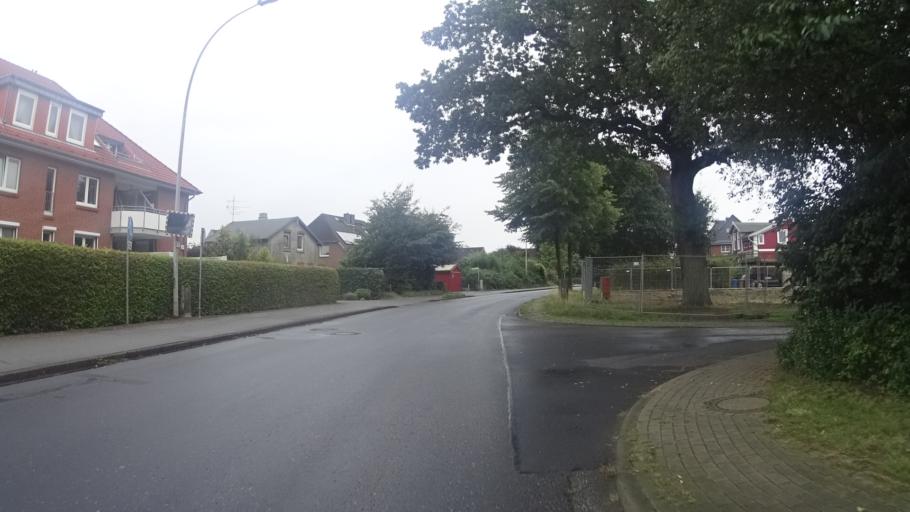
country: DE
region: Schleswig-Holstein
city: Kolln-Reisiek
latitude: 53.7575
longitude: 9.6975
